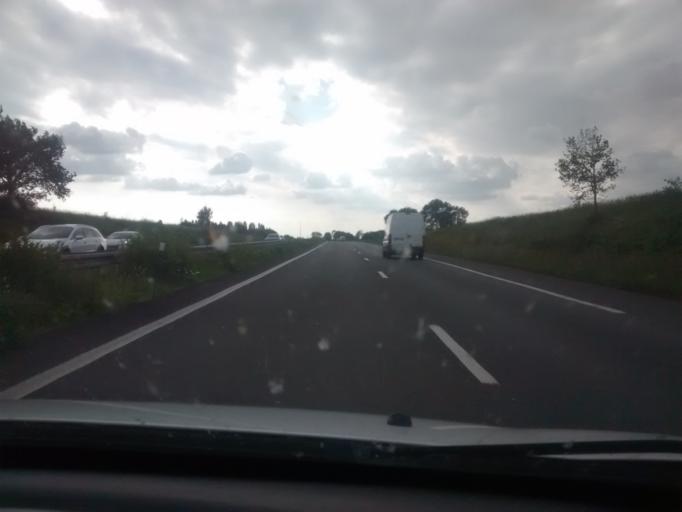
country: FR
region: Pays de la Loire
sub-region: Departement de la Mayenne
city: Soulge-sur-Ouette
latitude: 48.0663
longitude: -0.5417
